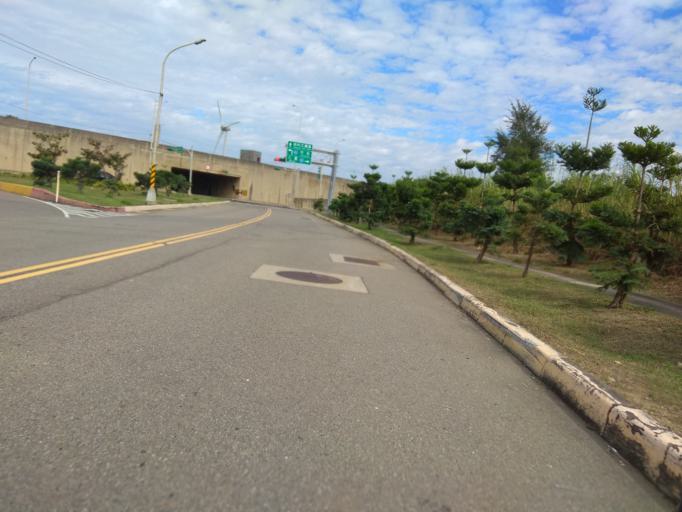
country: TW
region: Taiwan
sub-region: Hsinchu
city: Zhubei
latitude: 25.0397
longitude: 121.0726
